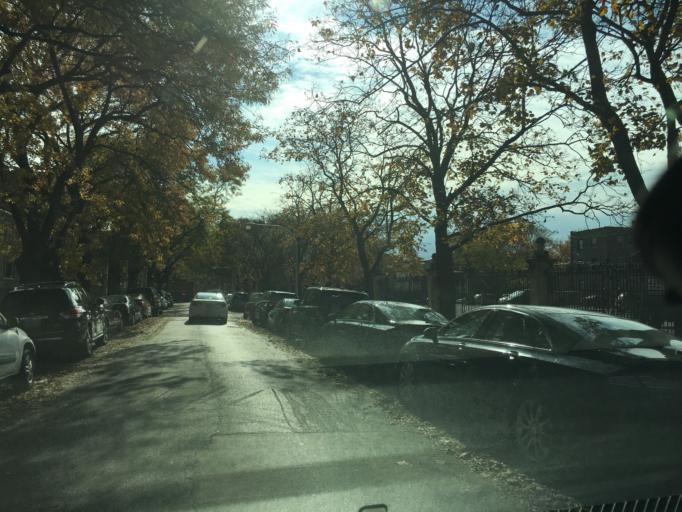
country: US
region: Illinois
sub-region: Cook County
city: Lincolnwood
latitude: 41.9967
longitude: -87.6972
